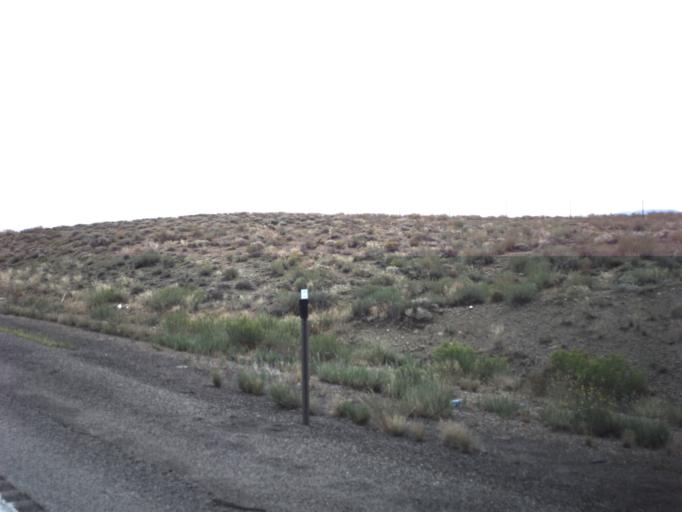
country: US
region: Utah
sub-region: Carbon County
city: Wellington
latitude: 39.5388
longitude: -110.6038
